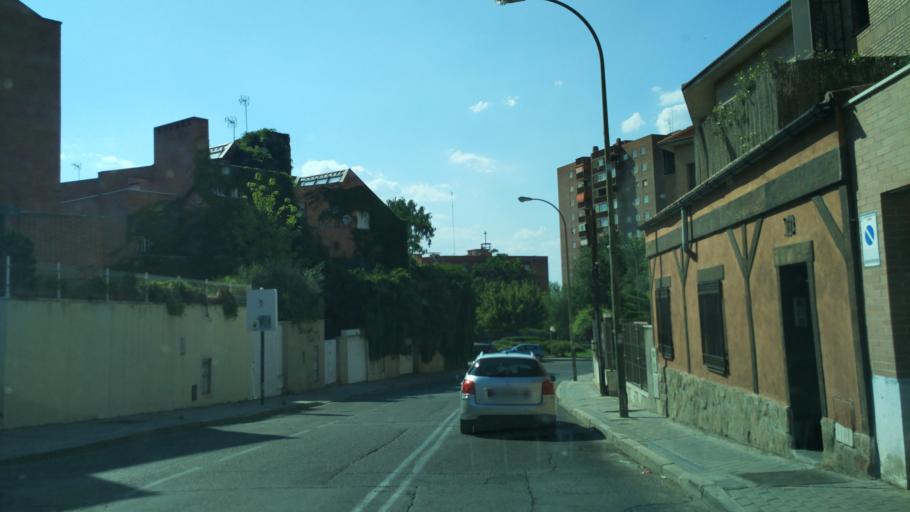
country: ES
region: Madrid
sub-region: Provincia de Madrid
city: Tetuan de las Victorias
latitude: 40.4630
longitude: -3.7204
